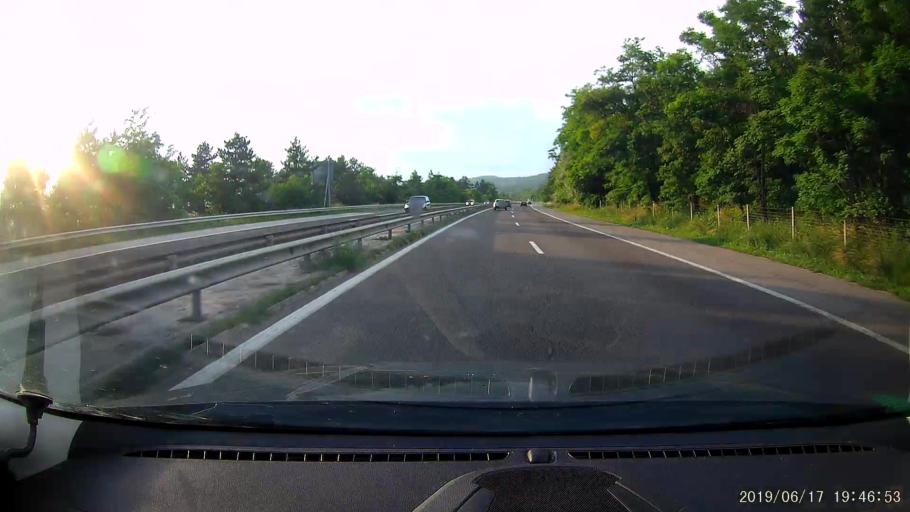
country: BG
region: Sofiya
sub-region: Obshtina Ikhtiman
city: Ikhtiman
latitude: 42.4378
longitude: 23.8500
